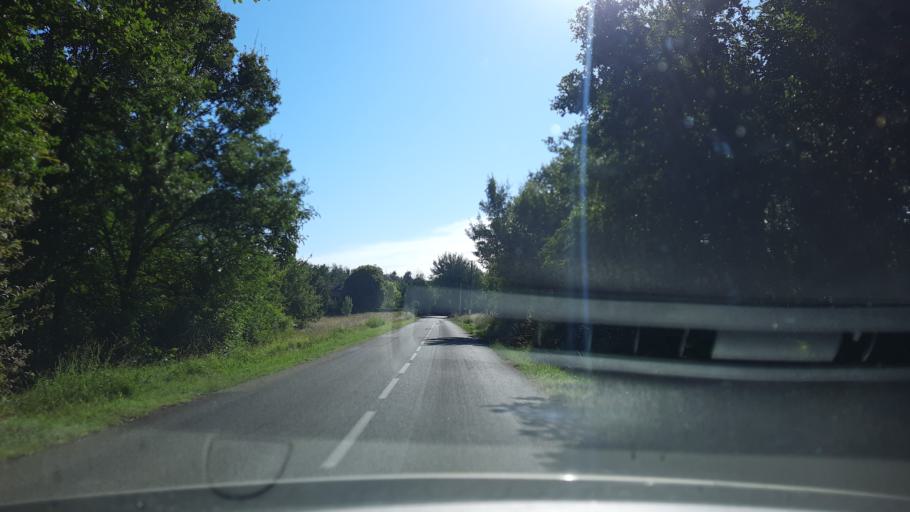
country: FR
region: Midi-Pyrenees
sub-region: Departement du Tarn-et-Garonne
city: Molieres
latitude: 44.1851
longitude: 1.3475
